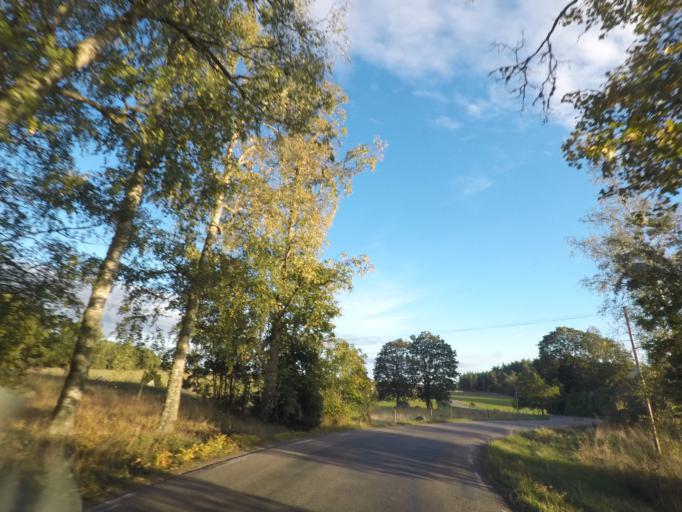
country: SE
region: Vaestmanland
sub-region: Kungsors Kommun
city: Kungsoer
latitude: 59.5071
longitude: 16.1090
